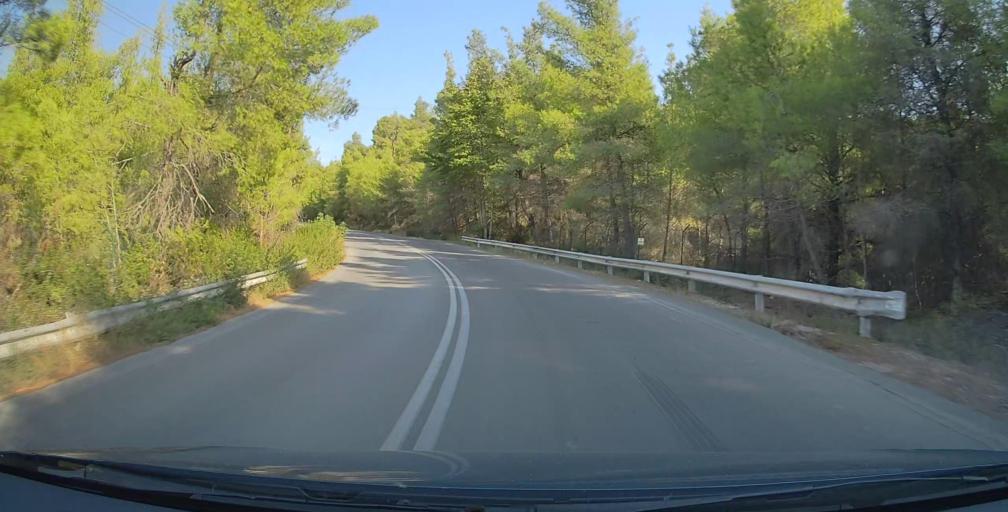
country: GR
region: Central Macedonia
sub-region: Nomos Chalkidikis
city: Neos Marmaras
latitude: 40.0650
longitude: 23.8040
